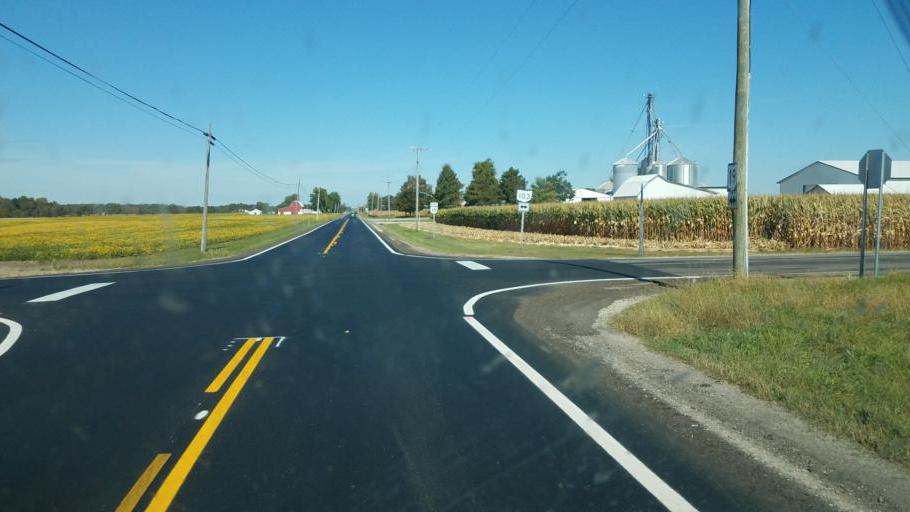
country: US
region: Ohio
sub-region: Crawford County
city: Bucyrus
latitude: 40.9501
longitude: -83.0164
